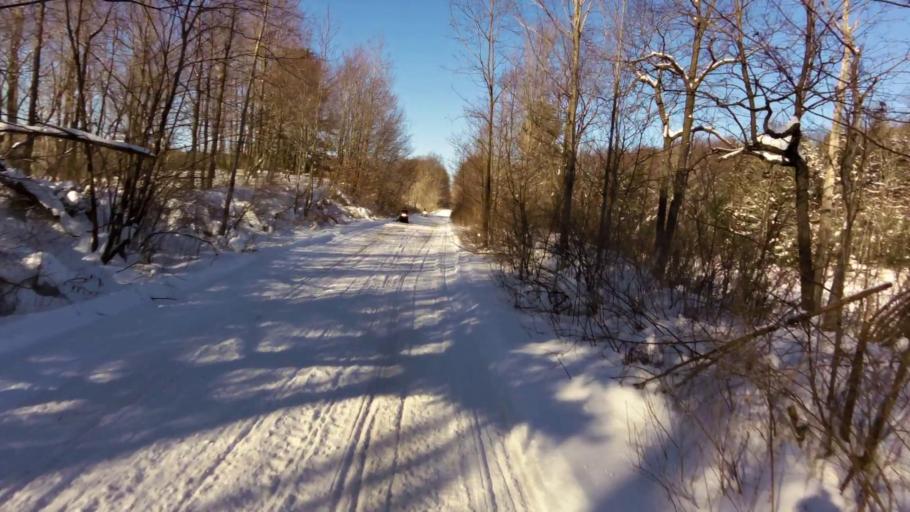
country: US
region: New York
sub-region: Chautauqua County
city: Mayville
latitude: 42.1797
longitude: -79.5811
